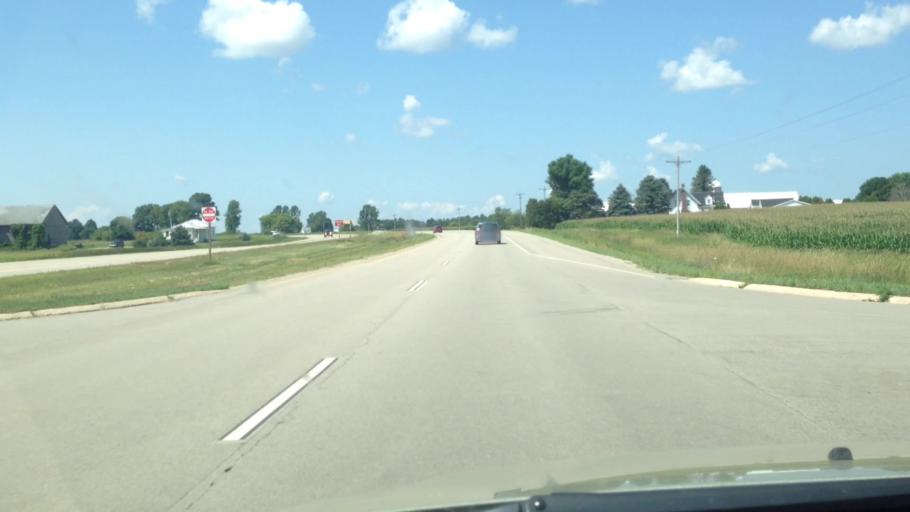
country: US
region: Wisconsin
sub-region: Oconto County
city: Oconto Falls
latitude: 44.8004
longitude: -88.0161
